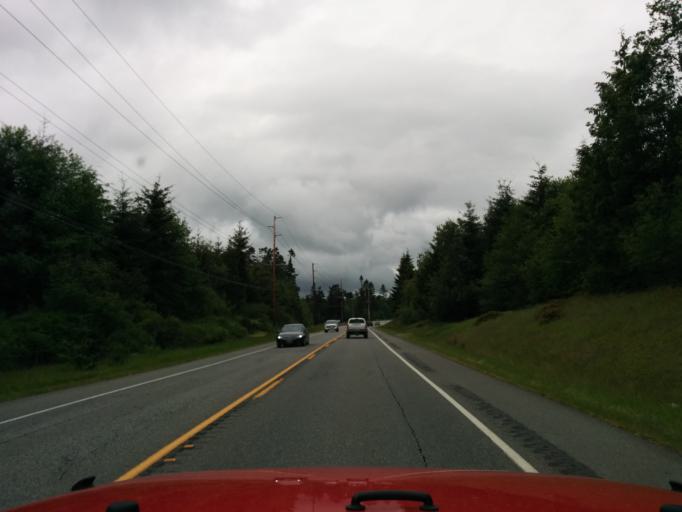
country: US
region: Washington
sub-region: Island County
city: Camano
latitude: 48.1605
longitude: -122.6042
